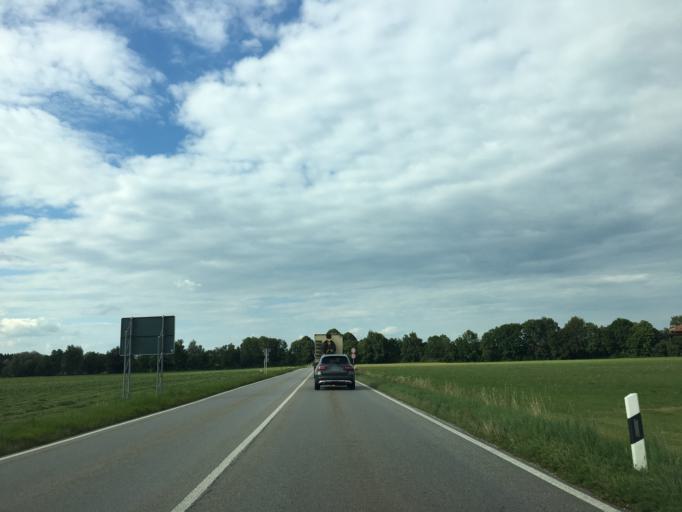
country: DE
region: Bavaria
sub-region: Upper Bavaria
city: Warngau
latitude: 47.8331
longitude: 11.7171
